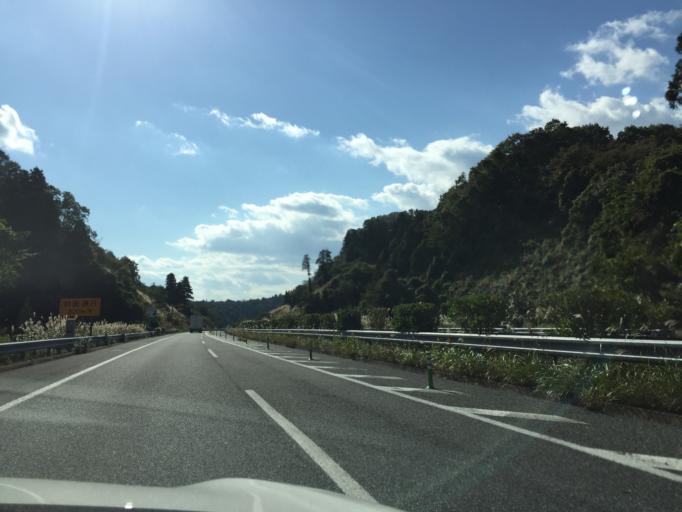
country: JP
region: Fukushima
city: Iwaki
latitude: 37.1860
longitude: 140.9838
